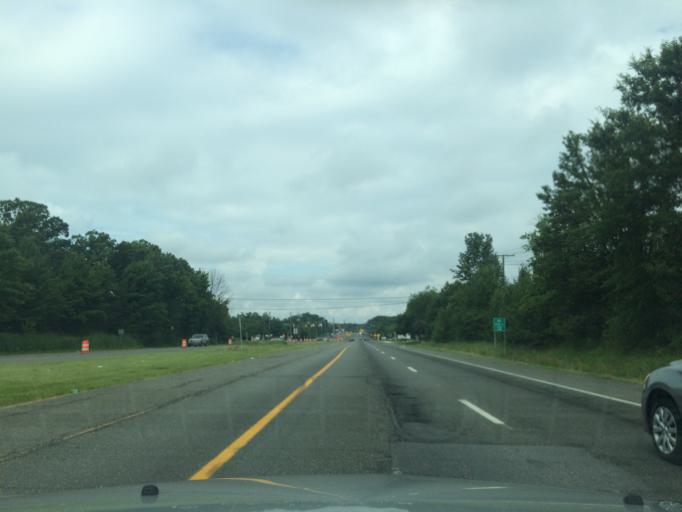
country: US
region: Maryland
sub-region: Prince George's County
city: Forestville
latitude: 38.8431
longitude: -76.8821
